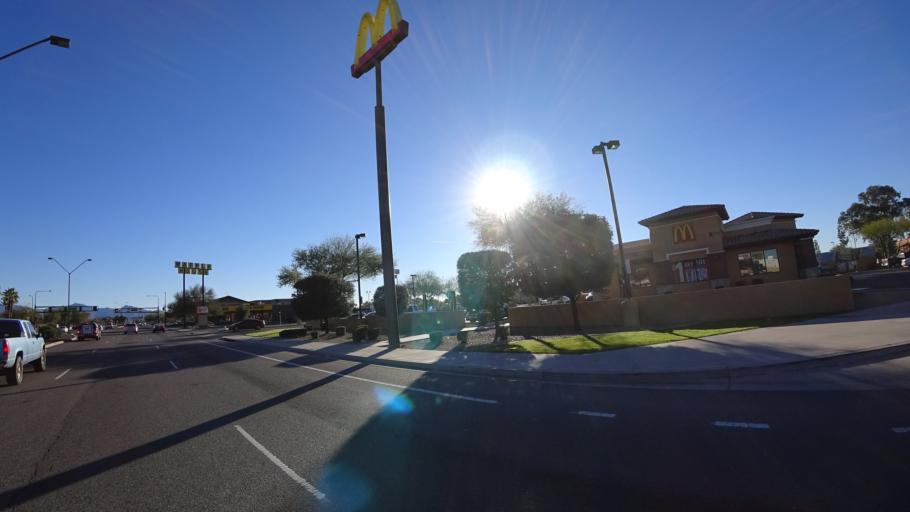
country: US
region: Arizona
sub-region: Maricopa County
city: Avondale
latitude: 33.4561
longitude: -112.3411
